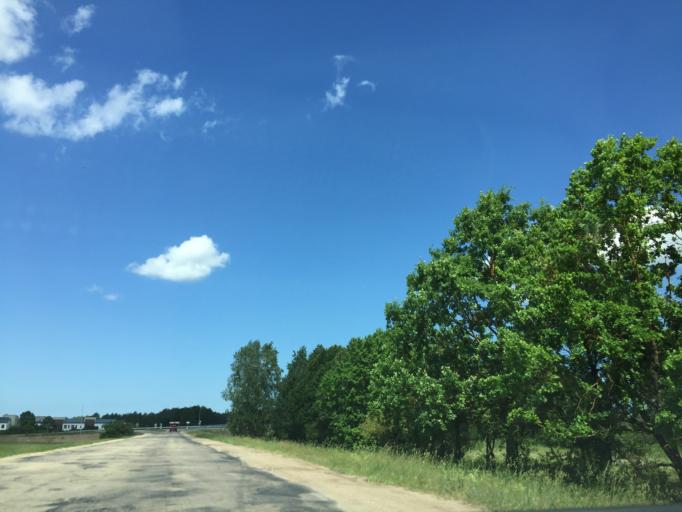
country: LV
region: Babite
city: Pinki
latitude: 56.8760
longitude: 23.9519
